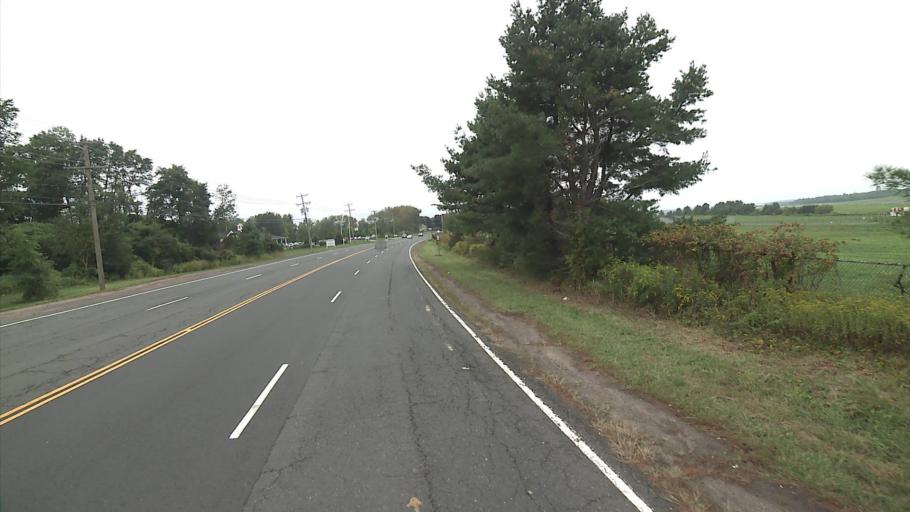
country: US
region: Connecticut
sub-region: Hartford County
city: Suffield Depot
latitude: 41.9533
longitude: -72.6651
